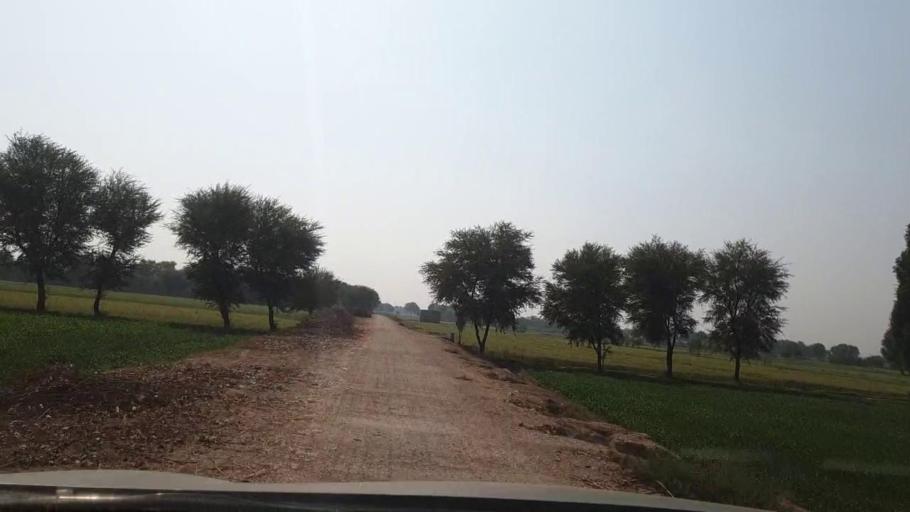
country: PK
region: Sindh
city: Tando Allahyar
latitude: 25.5313
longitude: 68.7901
